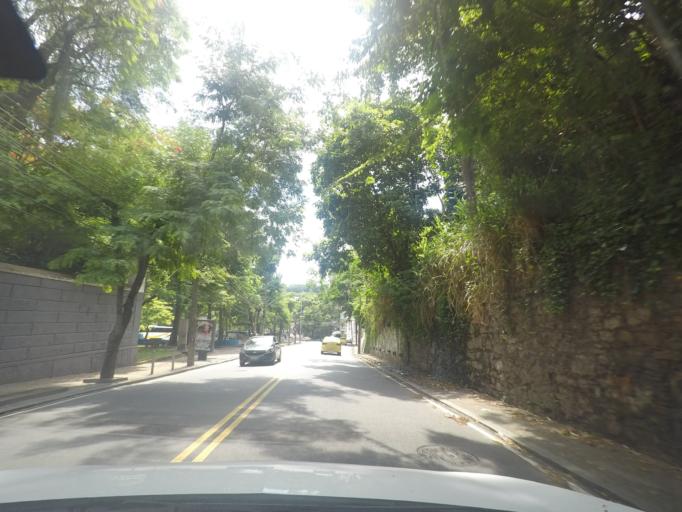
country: BR
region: Rio de Janeiro
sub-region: Rio De Janeiro
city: Rio de Janeiro
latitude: -22.9402
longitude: -43.2009
